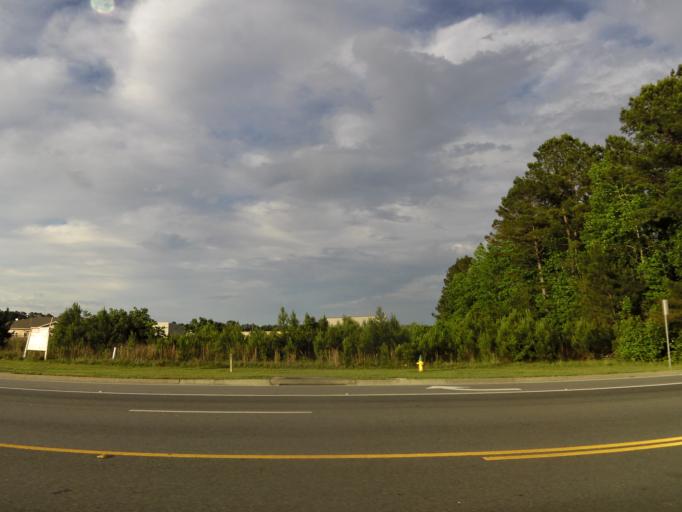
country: US
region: Georgia
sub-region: Chatham County
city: Pooler
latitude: 32.1022
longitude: -81.2241
